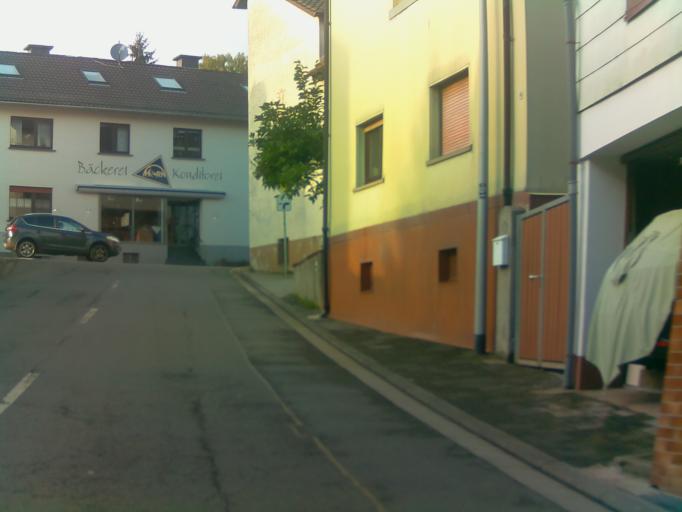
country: DE
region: Hesse
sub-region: Regierungsbezirk Darmstadt
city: Frankisch-Crumbach
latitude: 49.7445
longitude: 8.8538
